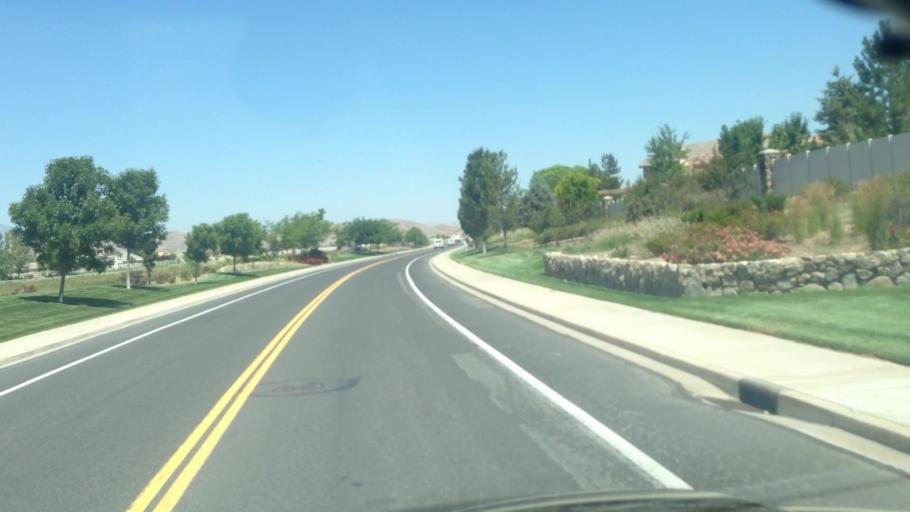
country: US
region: Nevada
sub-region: Washoe County
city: Sparks
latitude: 39.4284
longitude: -119.7156
